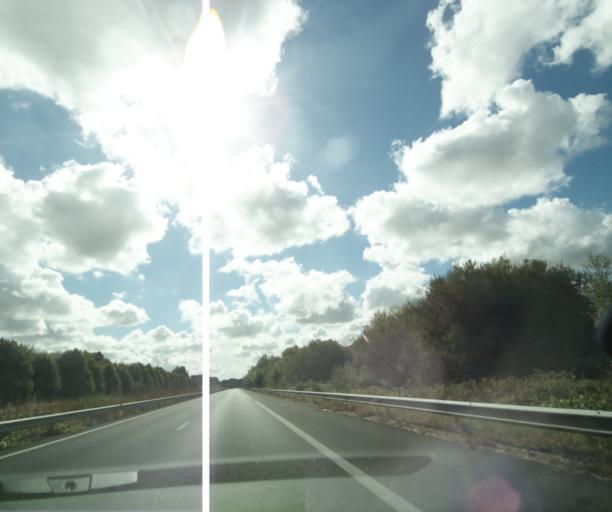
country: FR
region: Poitou-Charentes
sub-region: Departement de la Charente-Maritime
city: Cabariot
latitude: 45.9414
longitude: -0.8469
